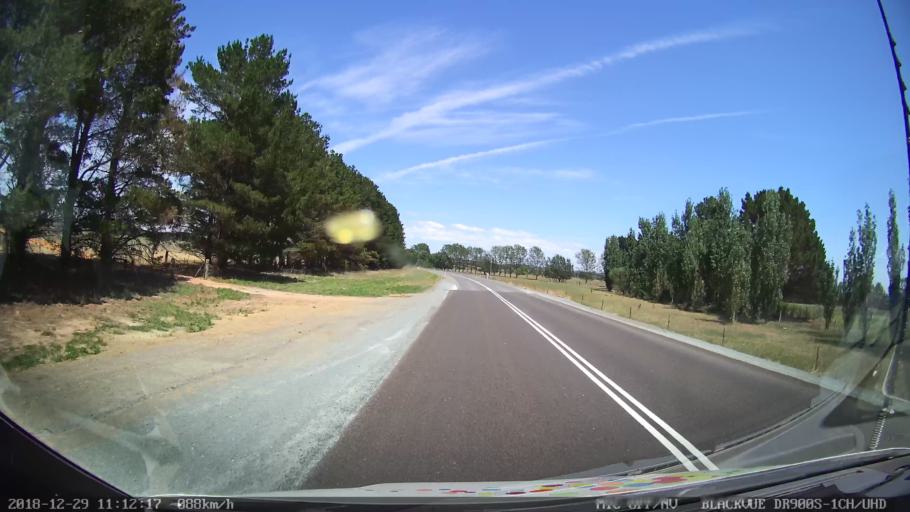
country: AU
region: New South Wales
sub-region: Palerang
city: Bungendore
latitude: -35.2117
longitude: 149.4783
